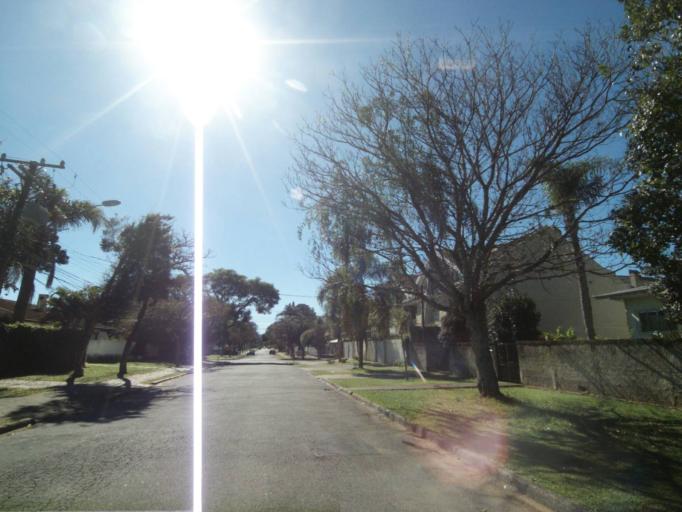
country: BR
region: Parana
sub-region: Curitiba
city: Curitiba
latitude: -25.4220
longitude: -49.2471
